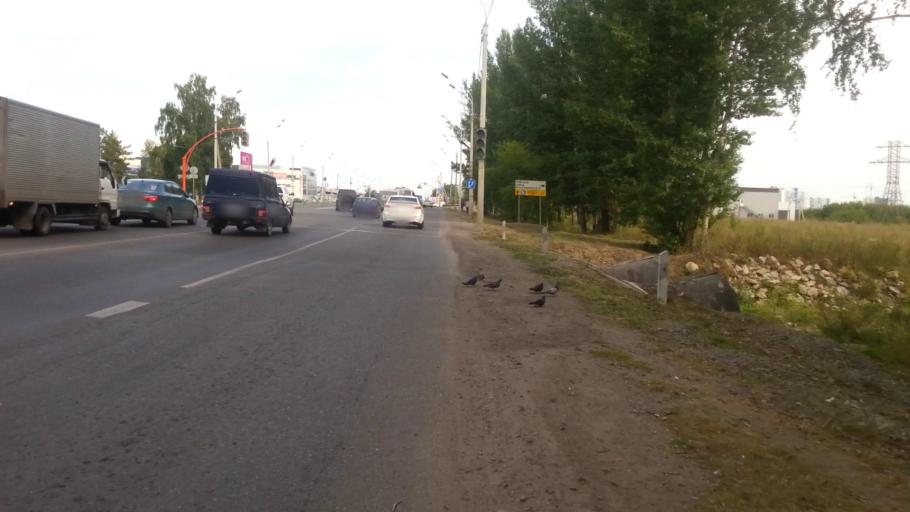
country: RU
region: Altai Krai
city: Novosilikatnyy
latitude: 53.3483
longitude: 83.6276
